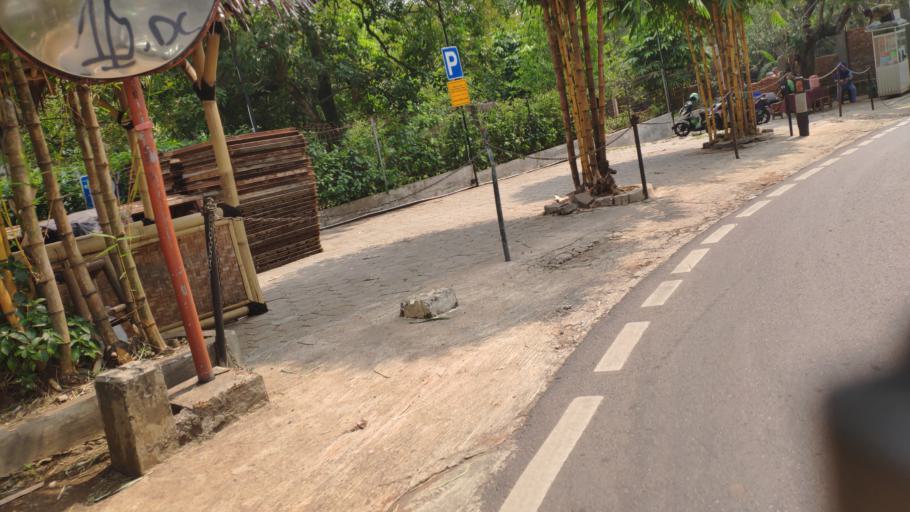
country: ID
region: West Java
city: Depok
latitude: -6.3171
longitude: 106.8181
